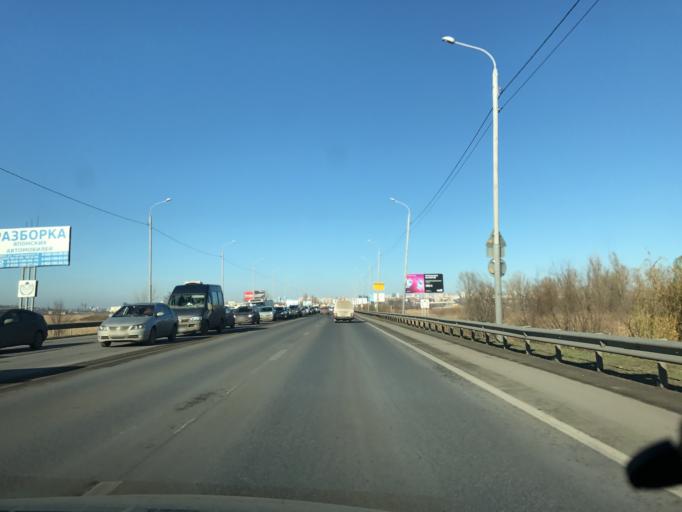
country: RU
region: Rostov
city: Bataysk
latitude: 47.1853
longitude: 39.7374
